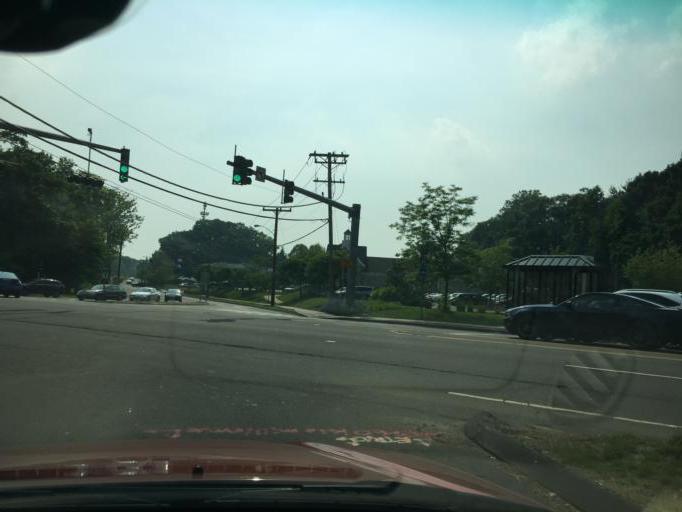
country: US
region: Connecticut
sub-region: Fairfield County
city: Darien
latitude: 41.0731
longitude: -73.4741
